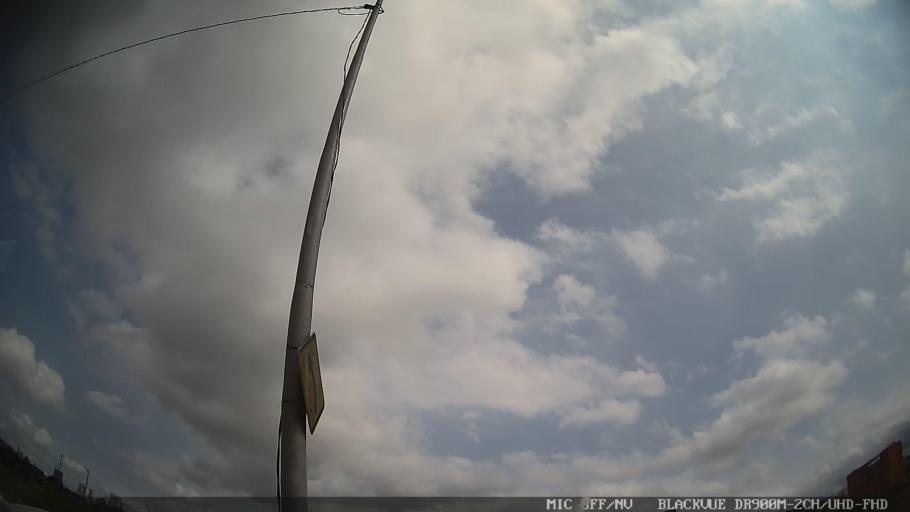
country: BR
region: Sao Paulo
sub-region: Taboao Da Serra
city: Taboao da Serra
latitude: -23.6634
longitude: -46.7275
